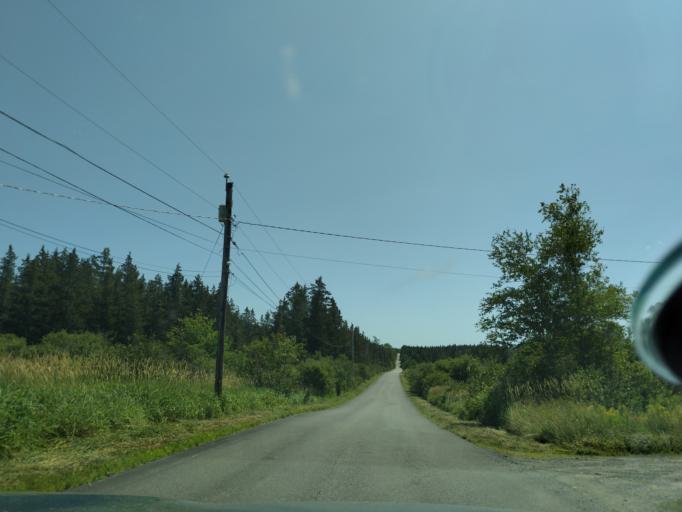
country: US
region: Maine
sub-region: Washington County
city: Eastport
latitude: 44.8390
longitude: -67.0135
